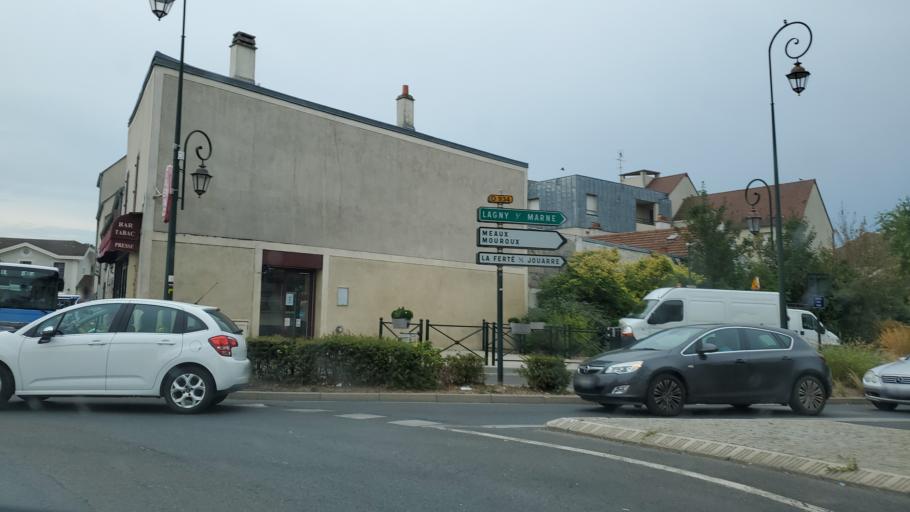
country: FR
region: Ile-de-France
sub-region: Departement de Seine-et-Marne
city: Coulommiers
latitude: 48.8087
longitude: 3.0827
